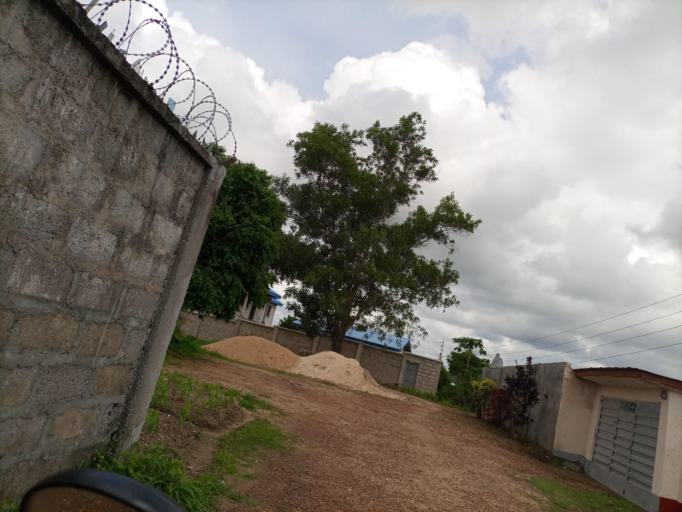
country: SL
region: Southern Province
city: Bo
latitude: 7.9729
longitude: -11.7651
